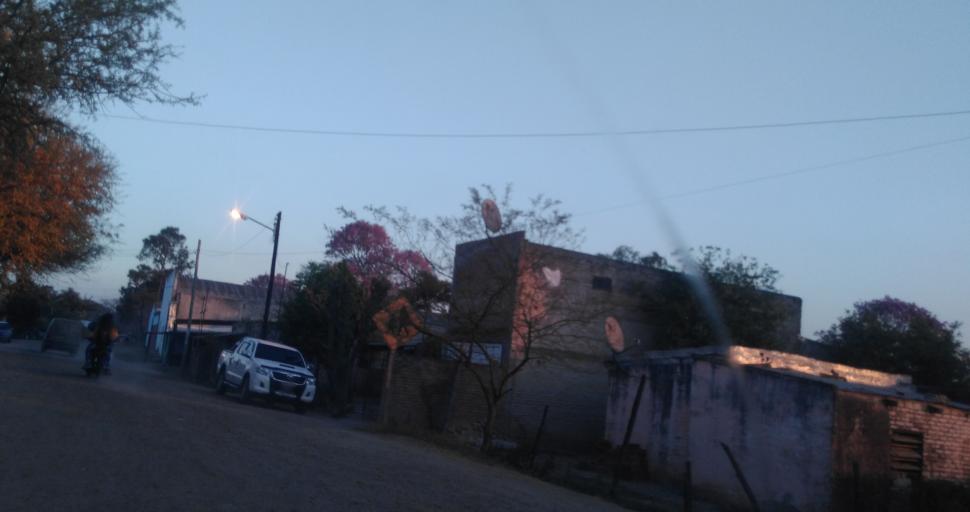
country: AR
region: Chaco
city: Resistencia
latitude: -27.4310
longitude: -58.9888
